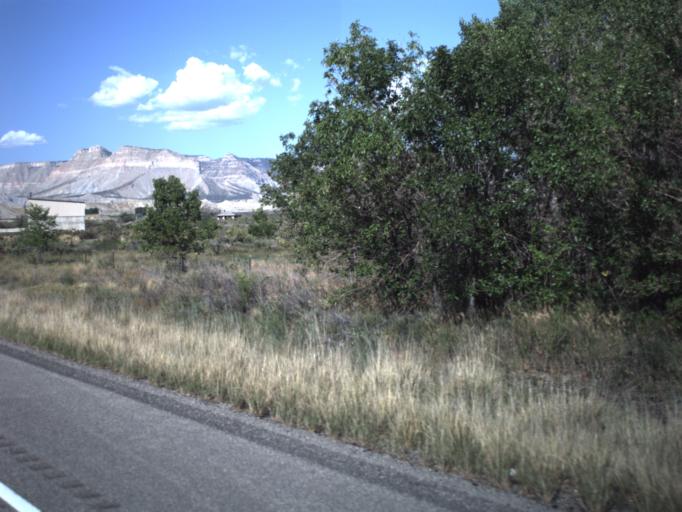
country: US
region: Utah
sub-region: Emery County
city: Orangeville
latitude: 39.1626
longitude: -111.0685
